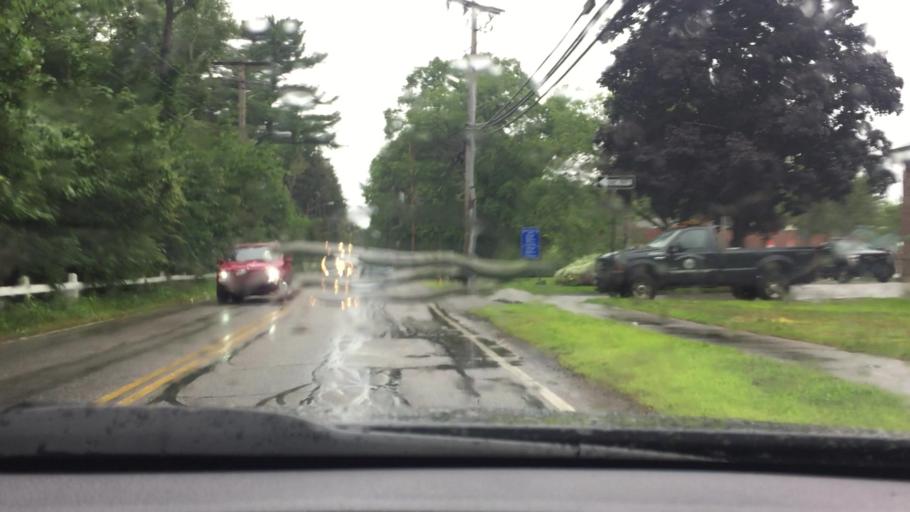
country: US
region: Massachusetts
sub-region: Norfolk County
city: Needham
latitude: 42.2695
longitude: -71.2209
